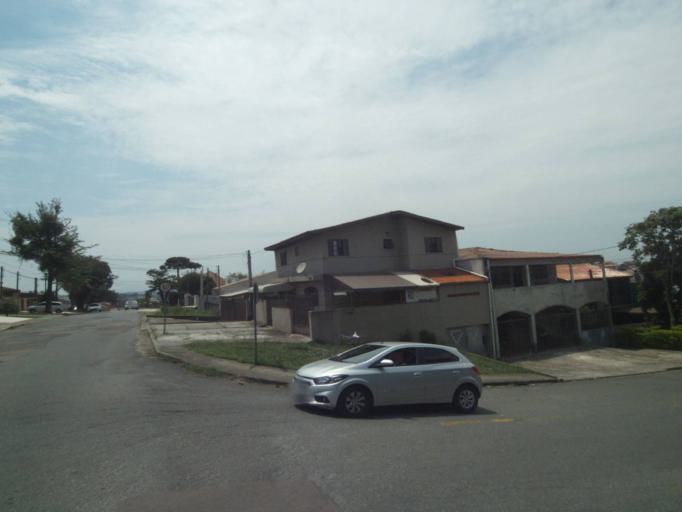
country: BR
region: Parana
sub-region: Pinhais
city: Pinhais
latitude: -25.3972
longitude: -49.2071
